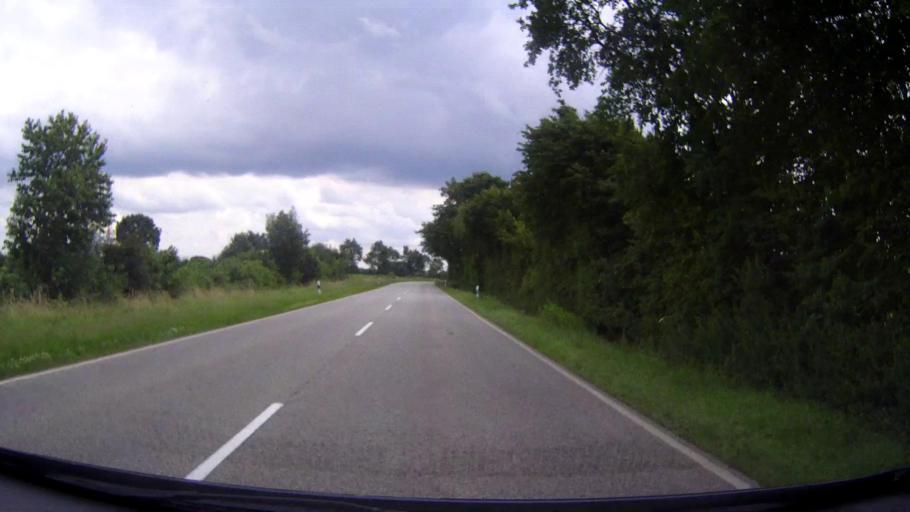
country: DE
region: Schleswig-Holstein
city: Schenefeld
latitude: 54.0650
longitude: 9.4733
